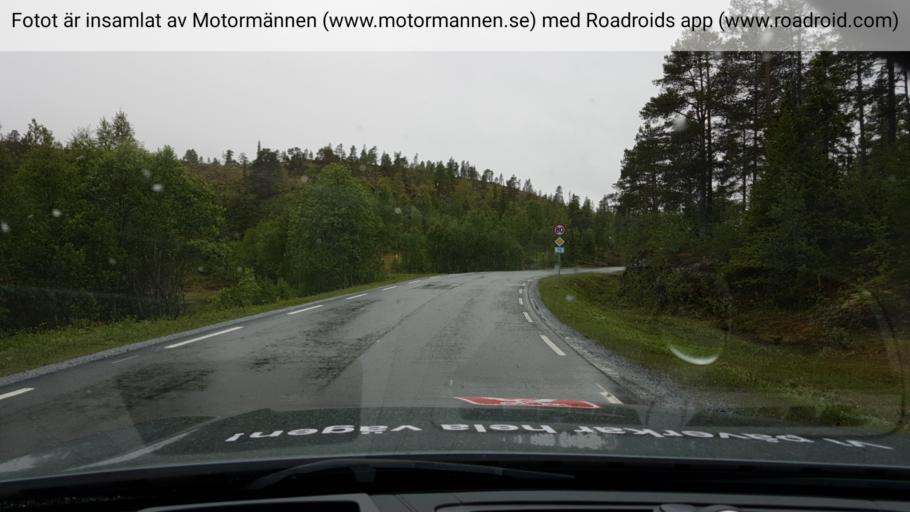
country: NO
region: Nord-Trondelag
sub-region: Snasa
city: Snaase
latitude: 63.6885
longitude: 12.3115
